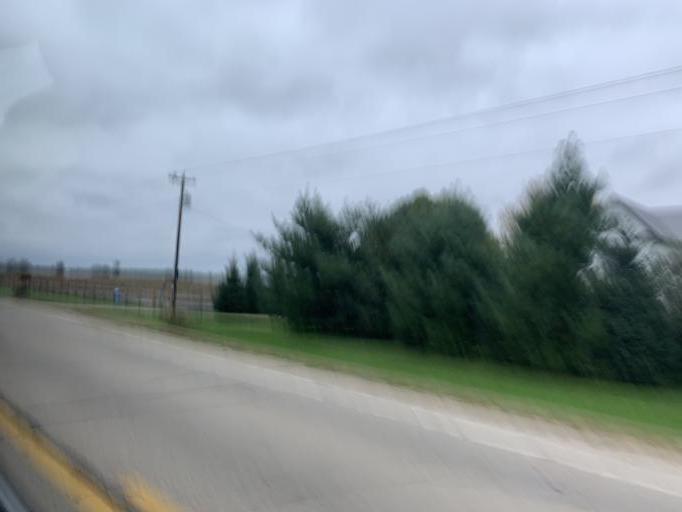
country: US
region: Wisconsin
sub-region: Grant County
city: Muscoda
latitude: 43.2198
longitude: -90.5229
